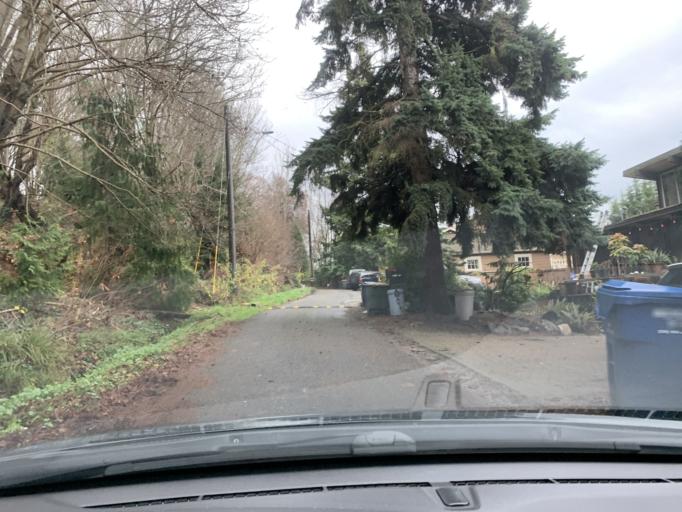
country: US
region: Washington
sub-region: King County
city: White Center
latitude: 47.5630
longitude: -122.4050
